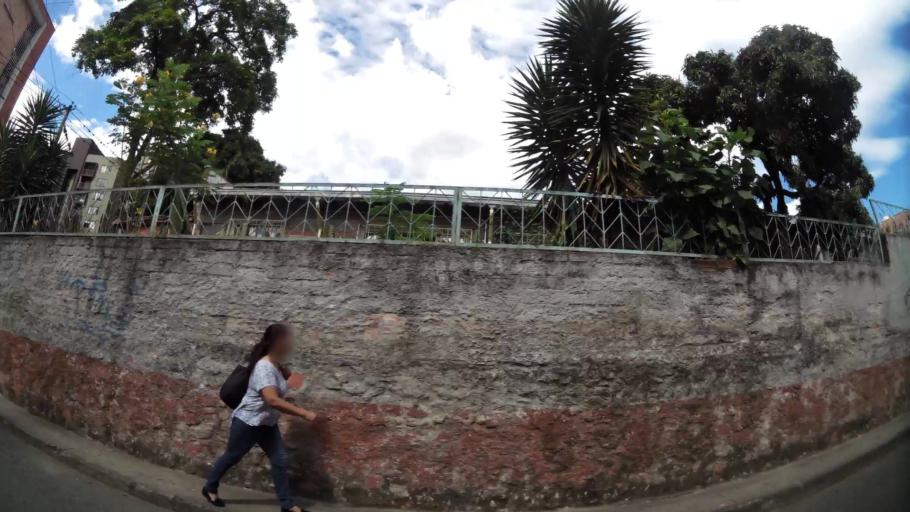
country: CO
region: Antioquia
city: Sabaneta
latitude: 6.1547
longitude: -75.6086
